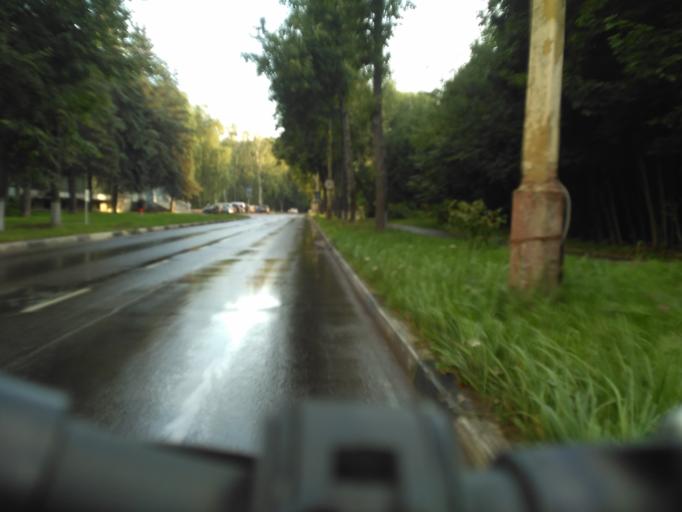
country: RU
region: Moskovskaya
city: Dubna
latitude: 56.7516
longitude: 37.1927
